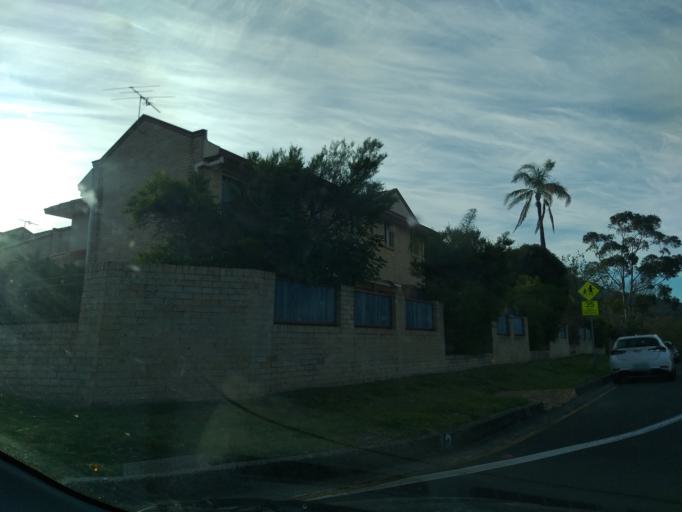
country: AU
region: New South Wales
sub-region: Wollongong
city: Mount Ousley
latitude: -34.3880
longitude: 150.8807
